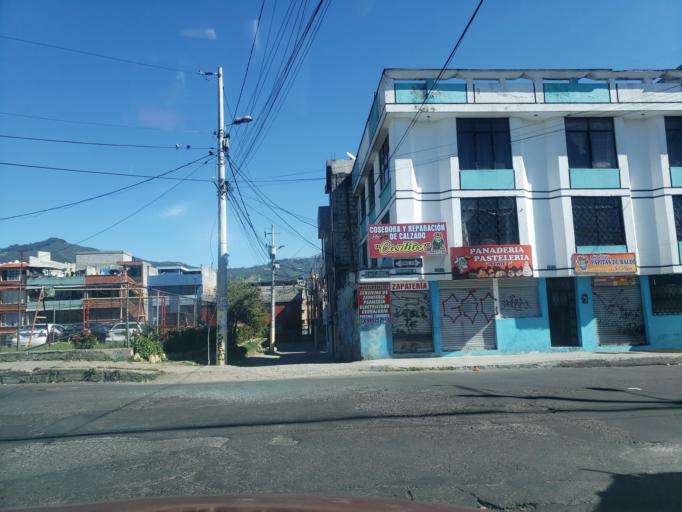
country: EC
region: Pichincha
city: Quito
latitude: -0.2714
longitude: -78.5401
